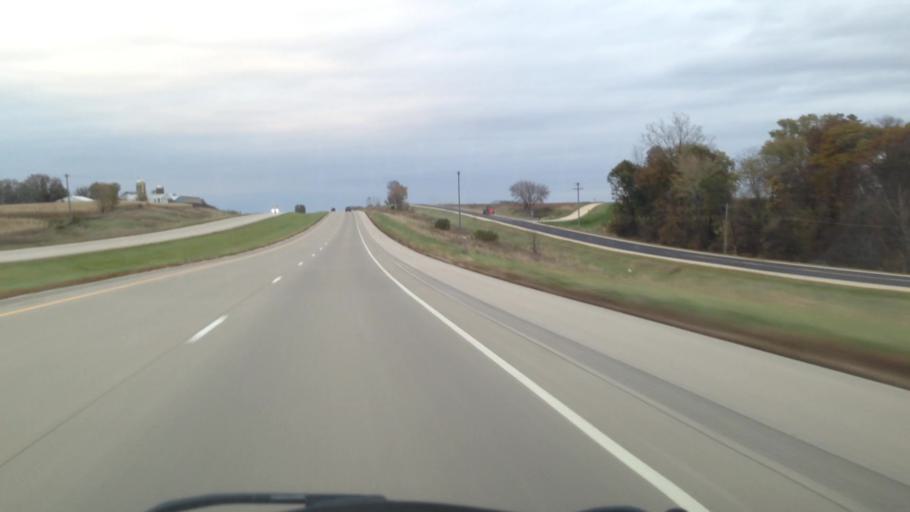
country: US
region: Wisconsin
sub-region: Trempealeau County
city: Trempealeau
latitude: 43.9191
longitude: -91.5030
